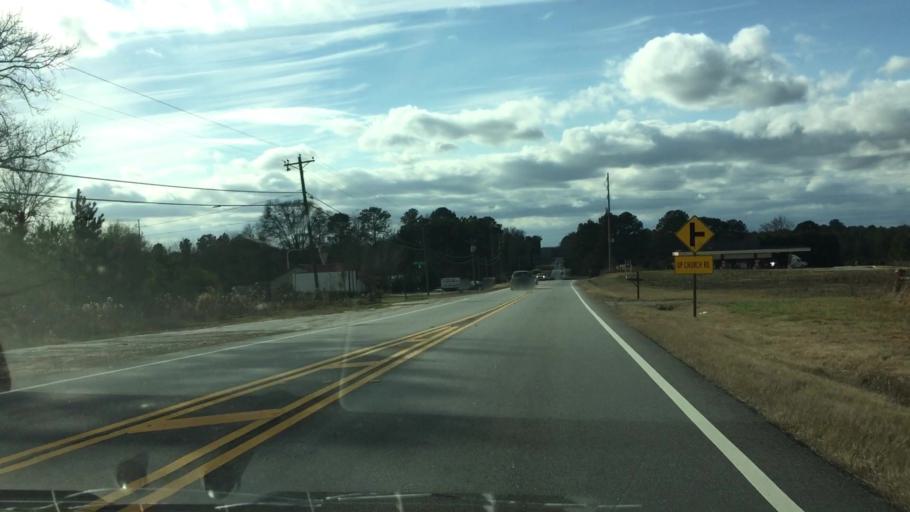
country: US
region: Georgia
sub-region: Henry County
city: McDonough
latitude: 33.4297
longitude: -84.0648
